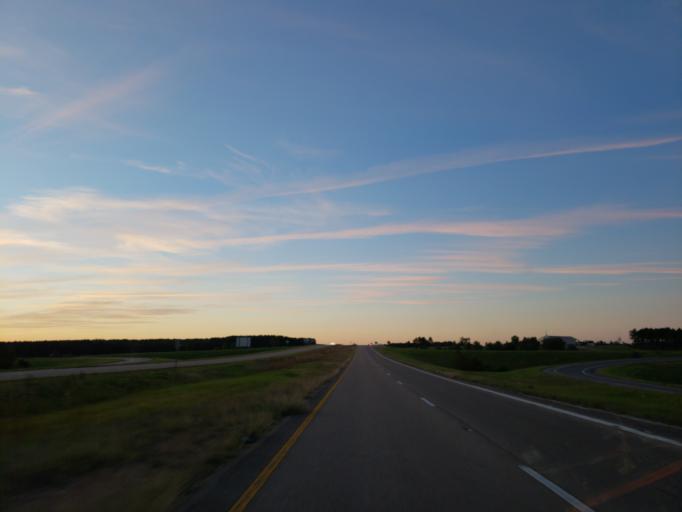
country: US
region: Mississippi
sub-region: Wayne County
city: Waynesboro
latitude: 31.7044
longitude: -88.6236
